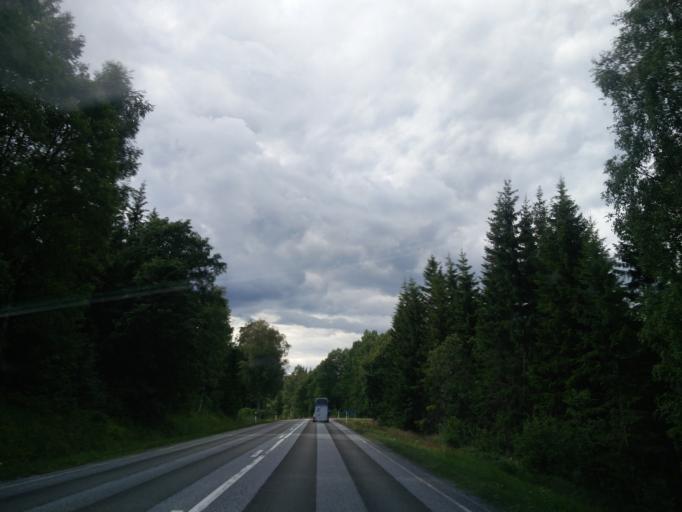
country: SE
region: OErebro
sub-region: Hallefors Kommun
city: Haellefors
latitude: 59.7632
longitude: 14.4220
